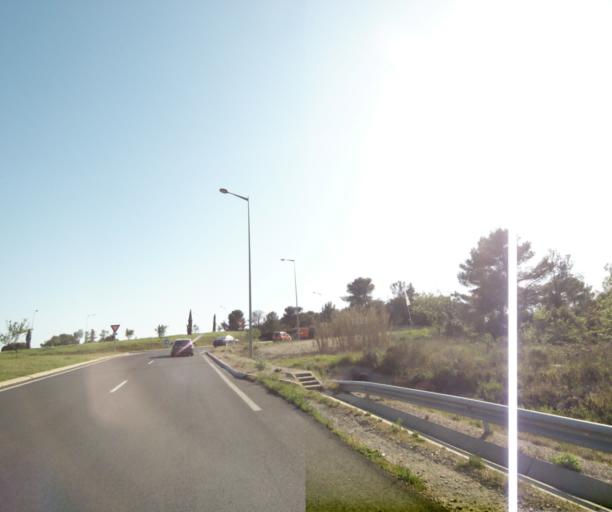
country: FR
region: Languedoc-Roussillon
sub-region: Departement de l'Herault
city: Jacou
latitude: 43.6527
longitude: 3.9213
